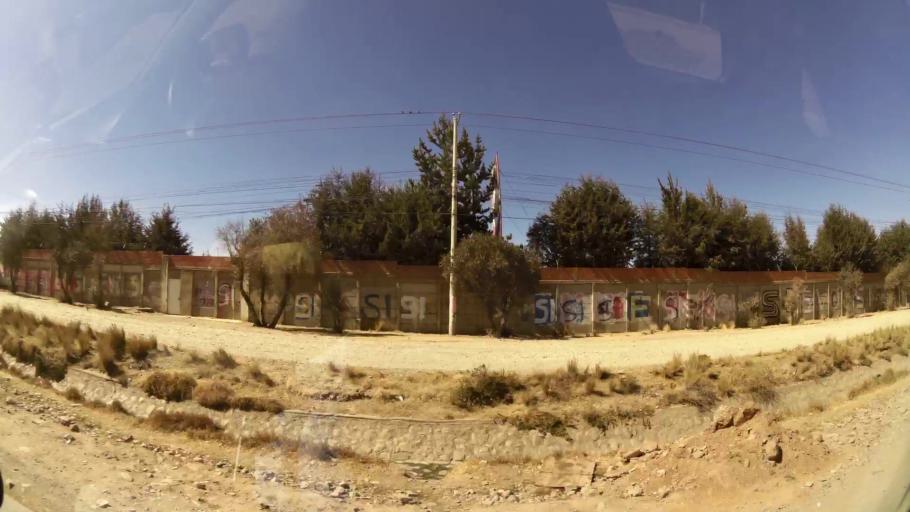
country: BO
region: La Paz
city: La Paz
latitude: -16.5481
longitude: -68.2032
